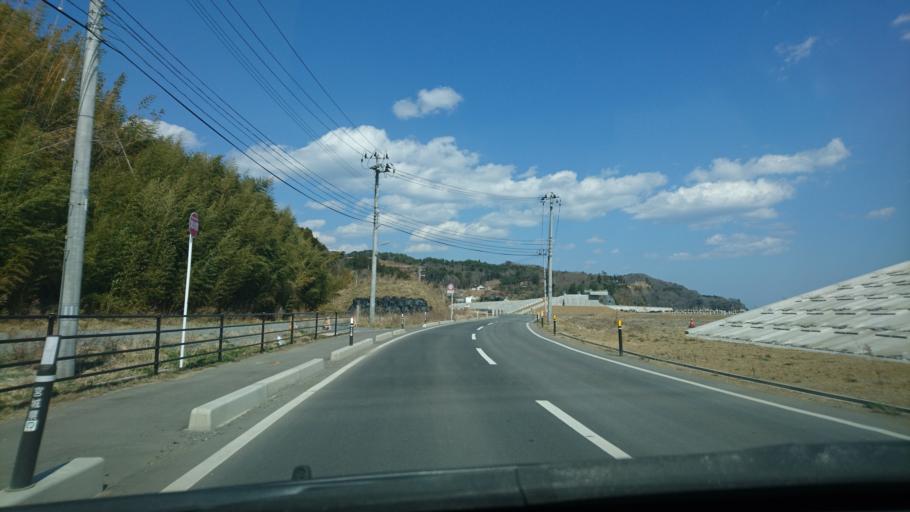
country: JP
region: Miyagi
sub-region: Oshika Gun
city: Onagawa Cho
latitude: 38.5800
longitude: 141.4604
